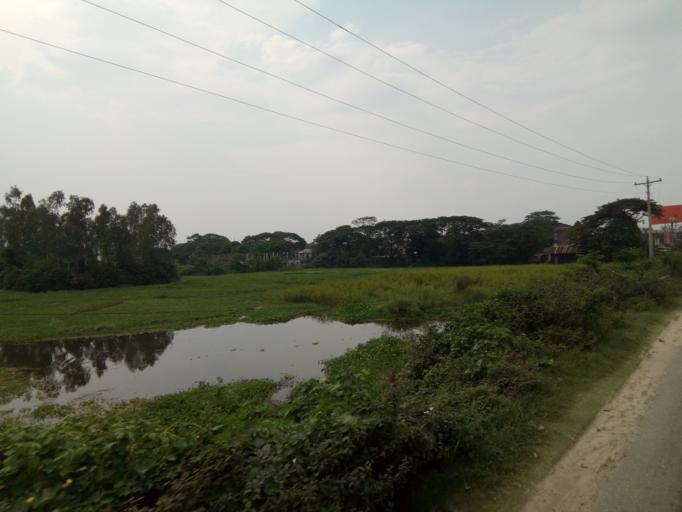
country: BD
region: Dhaka
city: Dohar
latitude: 23.5527
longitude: 90.2998
